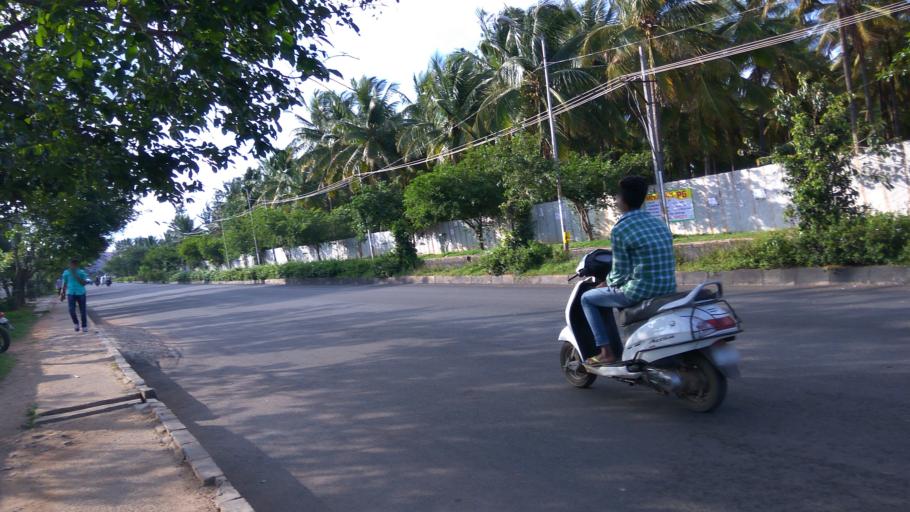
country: IN
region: Karnataka
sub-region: Bangalore Urban
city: Yelahanka
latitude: 13.1198
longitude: 77.6325
